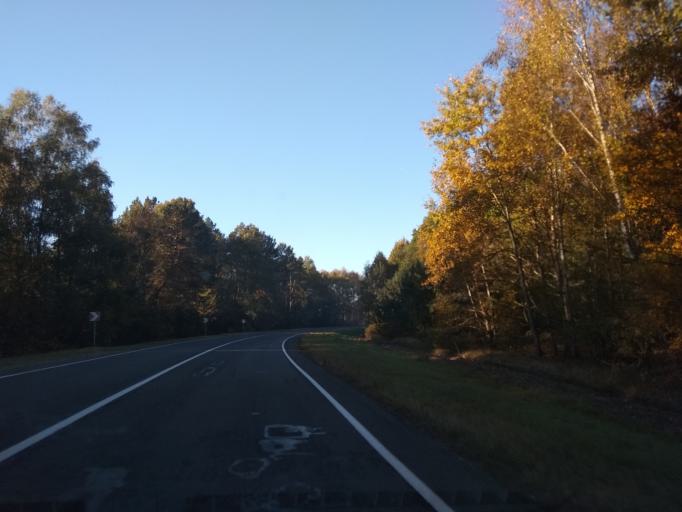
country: BY
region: Brest
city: Kobryn
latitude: 52.0334
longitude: 24.2695
